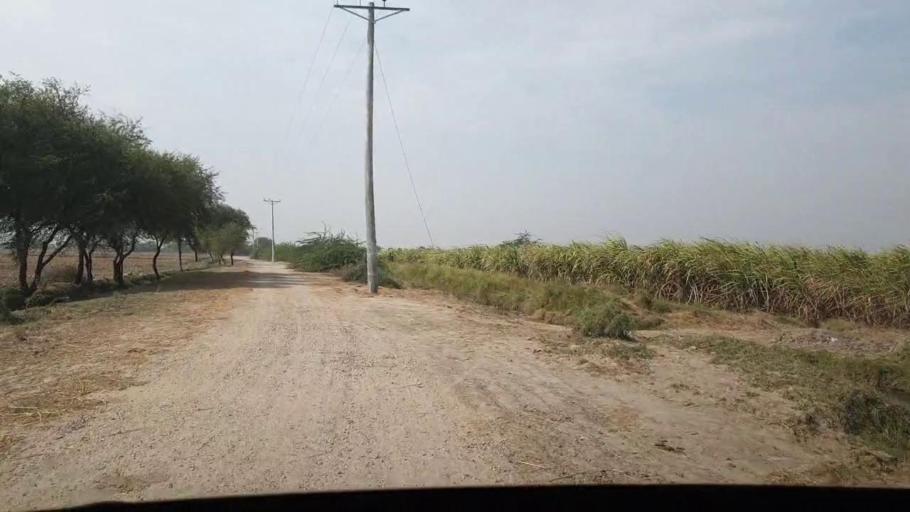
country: PK
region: Sindh
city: Chuhar Jamali
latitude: 24.3194
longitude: 67.9386
